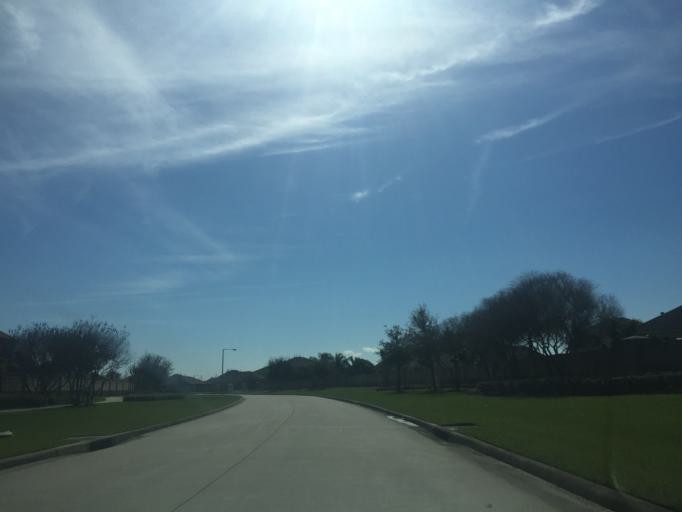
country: US
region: Texas
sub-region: Galveston County
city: Bacliff
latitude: 29.5131
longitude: -95.0199
